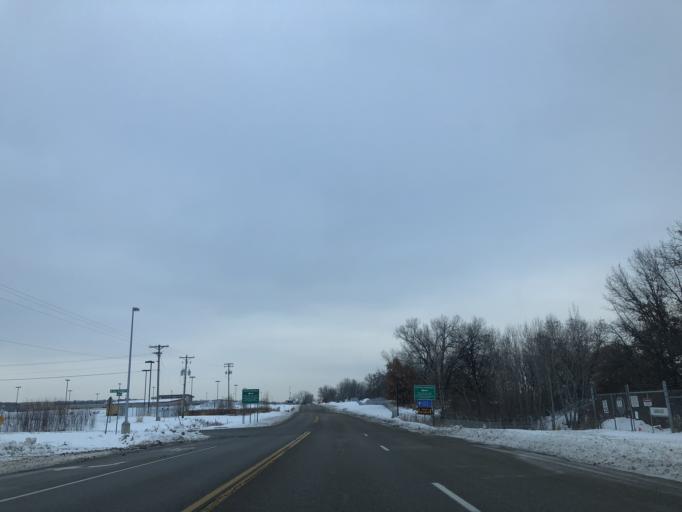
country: US
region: Minnesota
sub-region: Ramsey County
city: Shoreview
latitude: 45.0802
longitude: -93.1575
